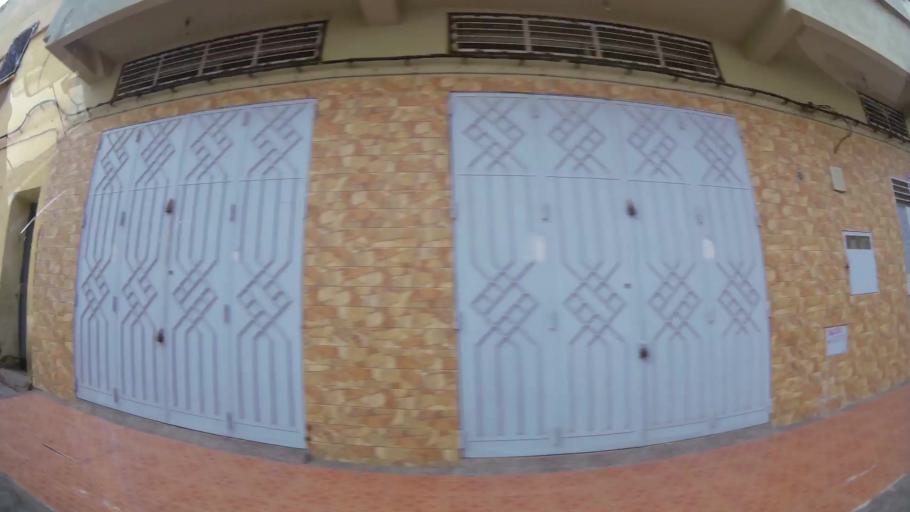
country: MA
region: Oriental
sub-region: Oujda-Angad
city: Oujda
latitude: 34.6863
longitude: -1.9112
